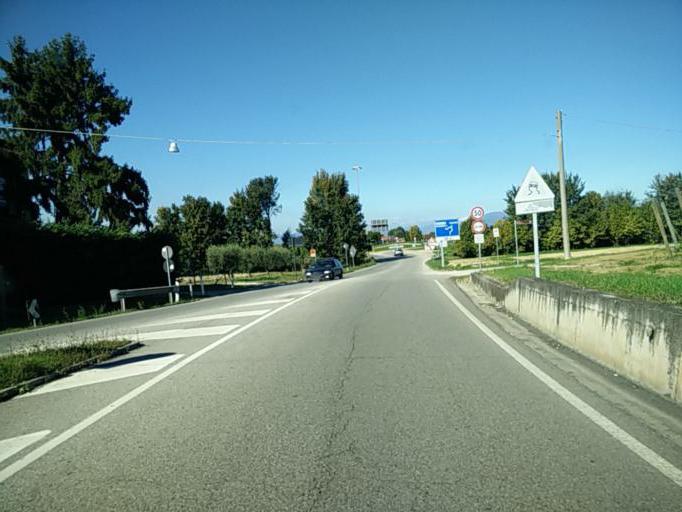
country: IT
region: Lombardy
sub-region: Provincia di Brescia
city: San Martino della Battaglia
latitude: 45.4457
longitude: 10.5952
